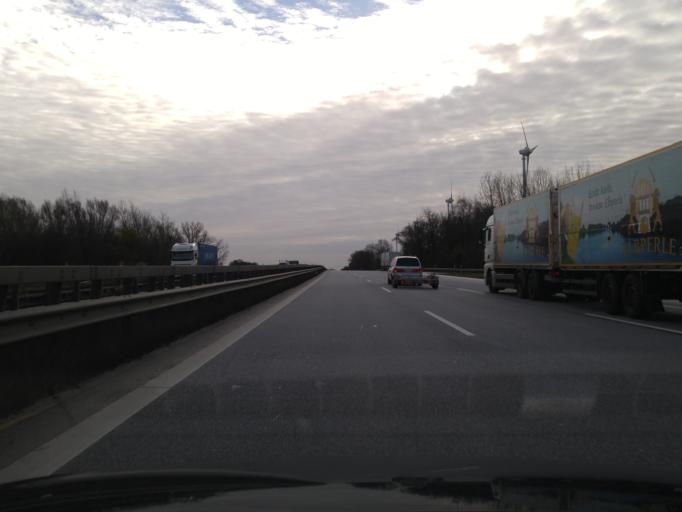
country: DE
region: Hamburg
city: Harburg
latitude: 53.4649
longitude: 10.0250
